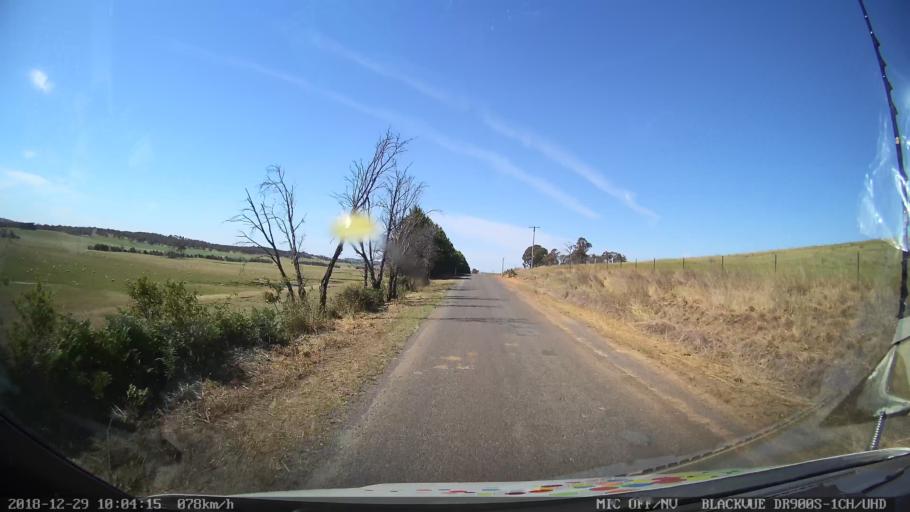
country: AU
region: New South Wales
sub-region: Goulburn Mulwaree
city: Goulburn
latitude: -34.8201
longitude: 149.4557
